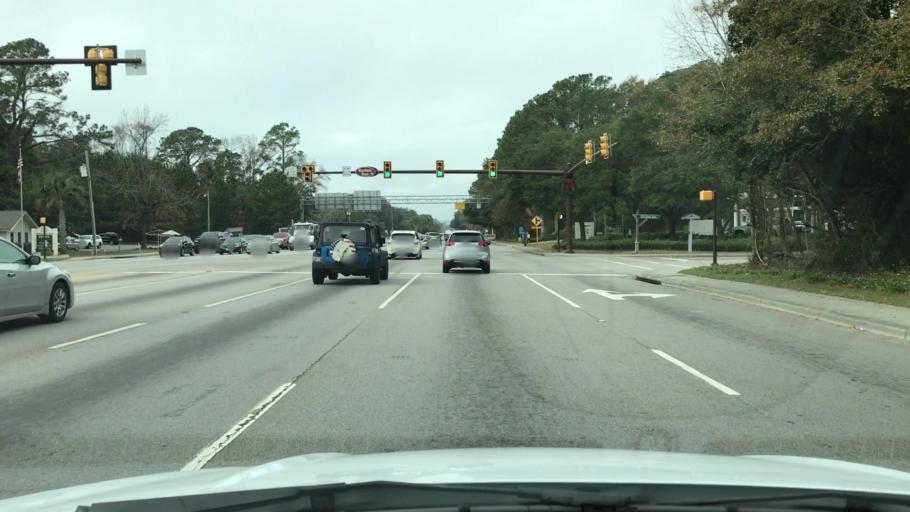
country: US
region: South Carolina
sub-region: Beaufort County
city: Hilton Head Island
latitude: 32.2155
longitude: -80.7471
